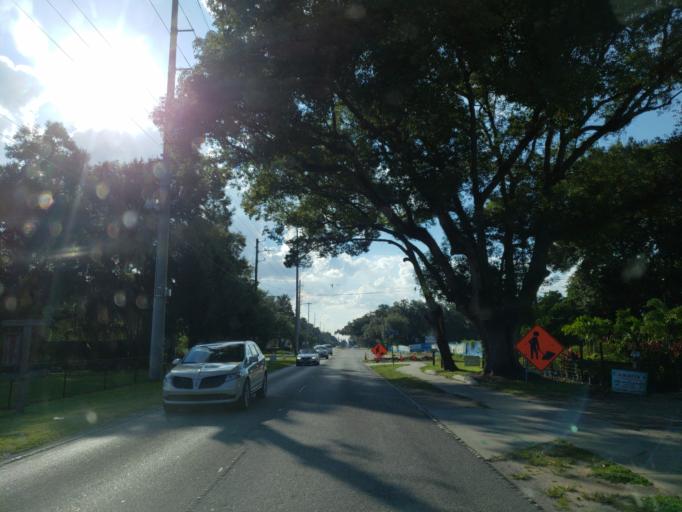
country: US
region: Florida
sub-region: Hillsborough County
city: Bloomingdale
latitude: 27.8937
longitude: -82.2397
